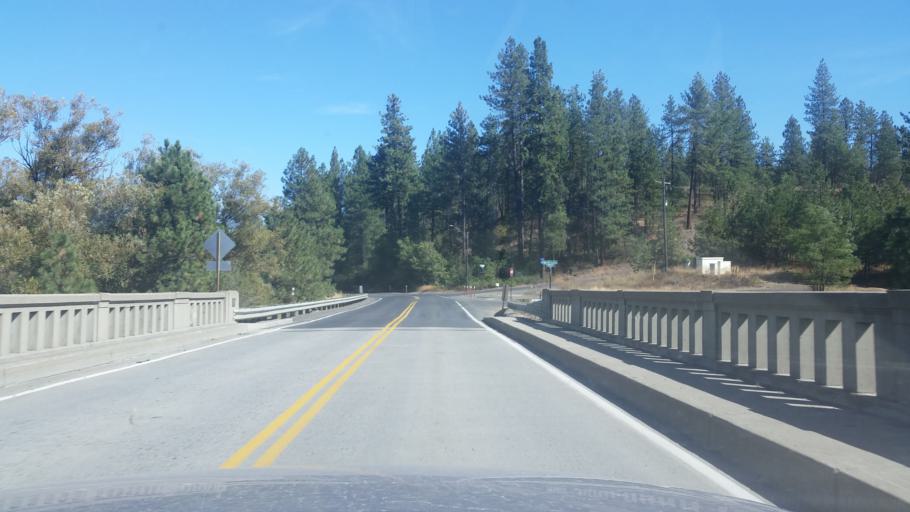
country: US
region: Washington
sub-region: Spokane County
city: Spokane
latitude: 47.5668
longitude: -117.4924
